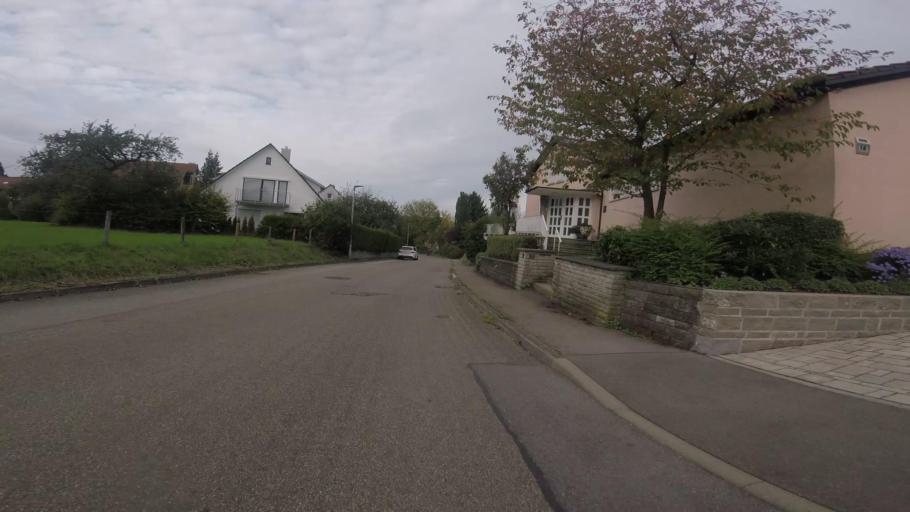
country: DE
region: Baden-Wuerttemberg
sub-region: Regierungsbezirk Stuttgart
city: Backnang
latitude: 48.9536
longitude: 9.4268
